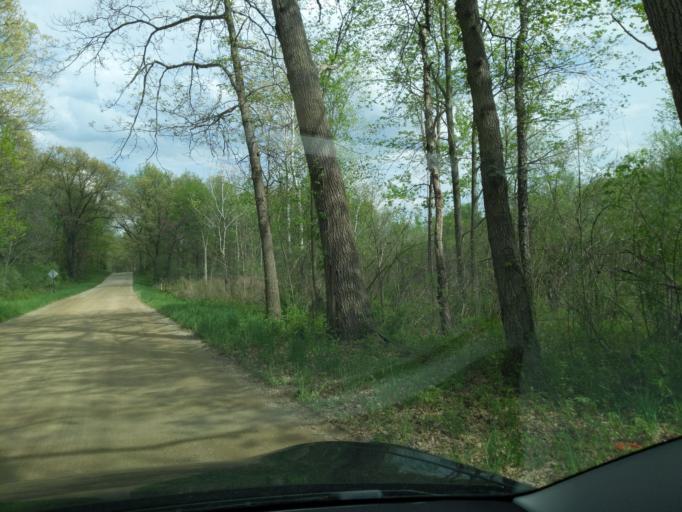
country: US
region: Michigan
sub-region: Washtenaw County
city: Chelsea
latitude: 42.4096
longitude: -84.0672
